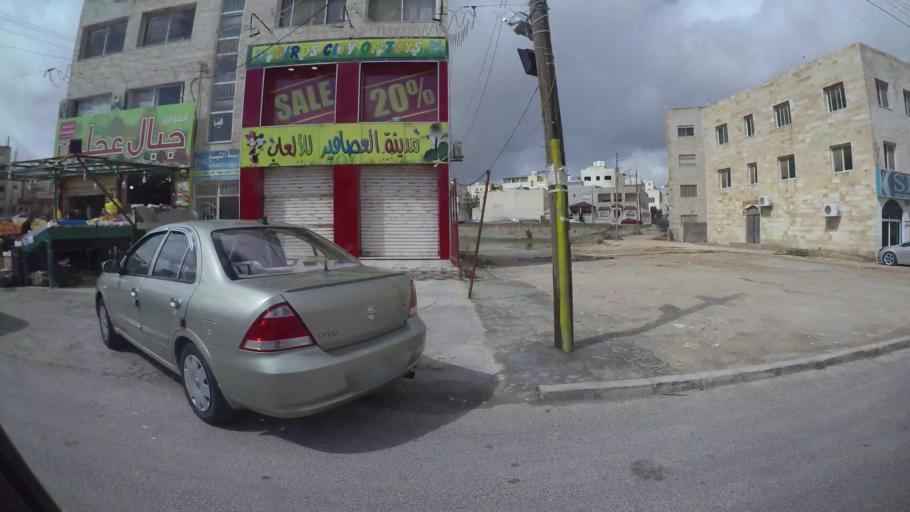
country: JO
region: Amman
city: Al Jubayhah
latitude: 32.0615
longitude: 35.8779
